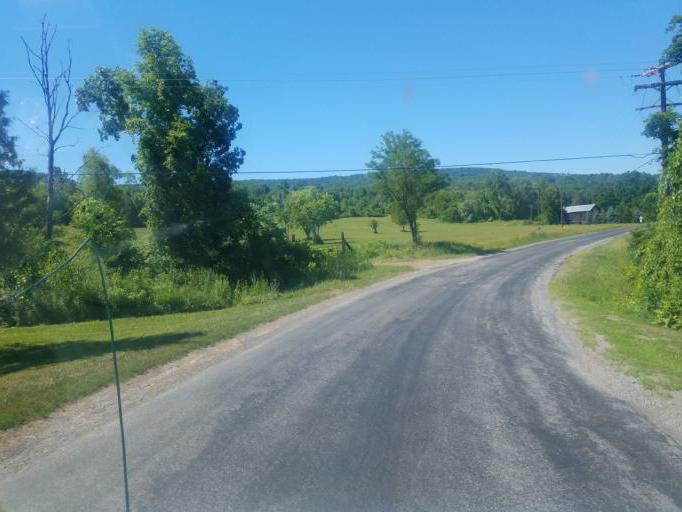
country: US
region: New York
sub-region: Ontario County
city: Naples
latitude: 42.7250
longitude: -77.3029
